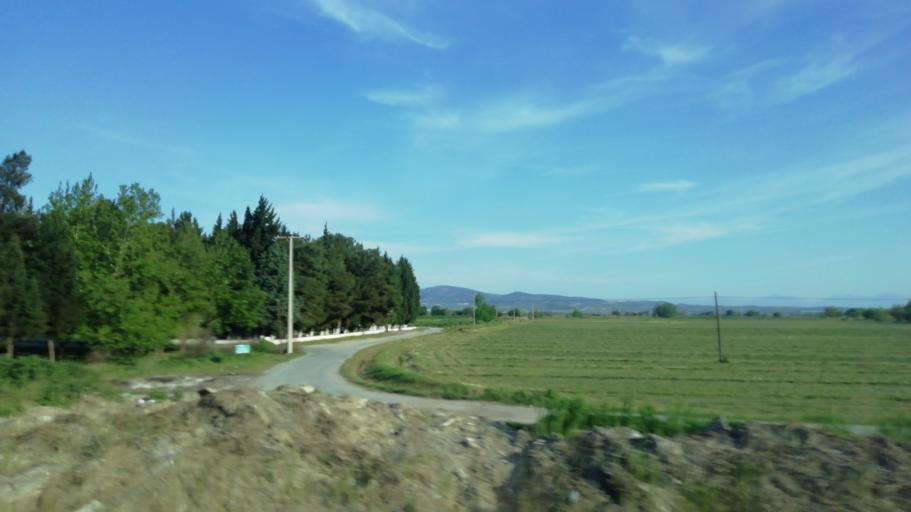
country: TR
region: Manisa
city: Saruhanli
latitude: 38.7460
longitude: 27.6137
